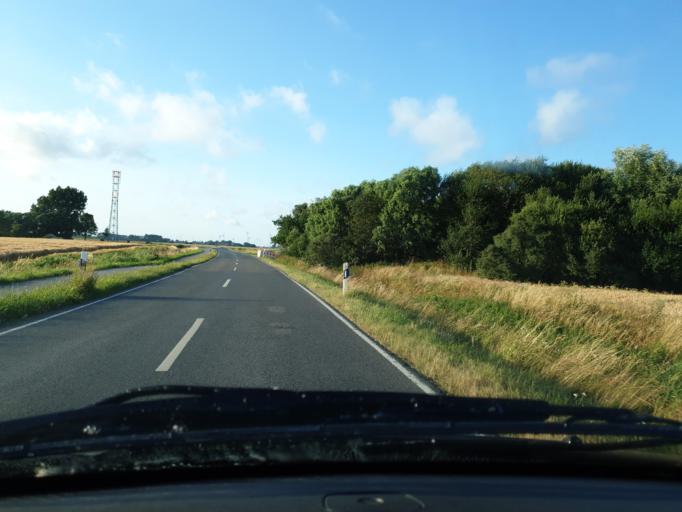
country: DE
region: Schleswig-Holstein
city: Wesselburener Deichhausen
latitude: 54.1492
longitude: 8.9174
